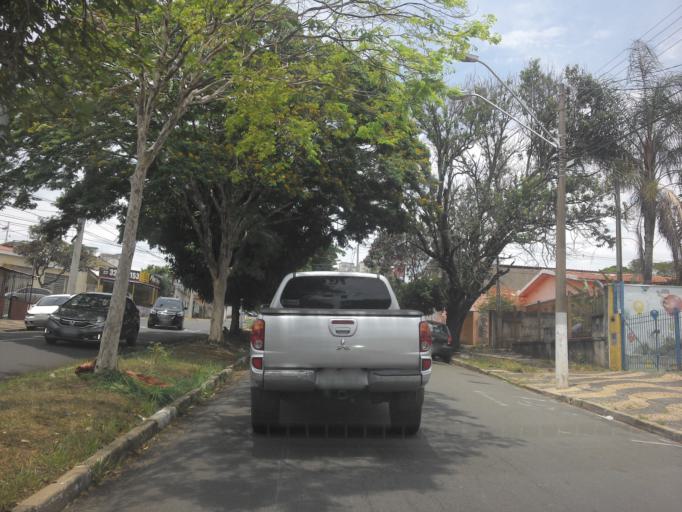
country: BR
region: Sao Paulo
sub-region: Campinas
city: Campinas
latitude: -22.9237
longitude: -47.0409
